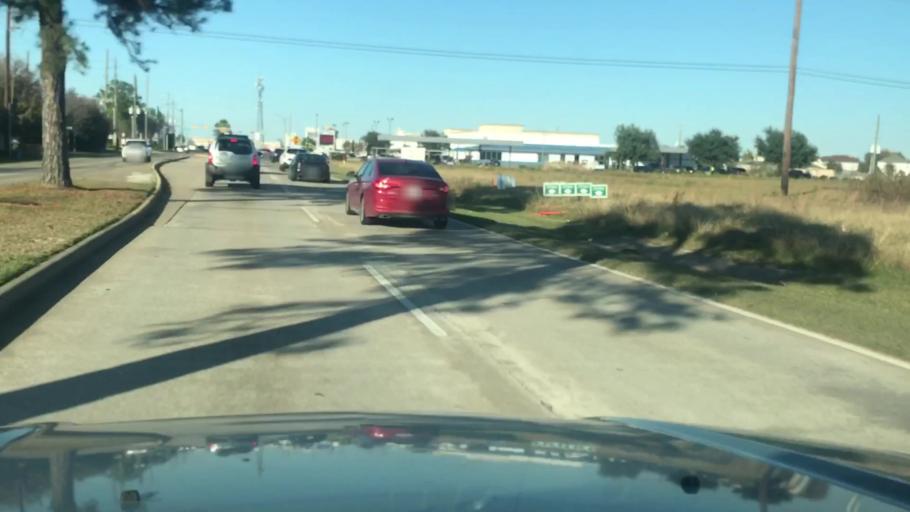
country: US
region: Texas
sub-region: Fort Bend County
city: Cinco Ranch
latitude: 29.8478
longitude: -95.7191
